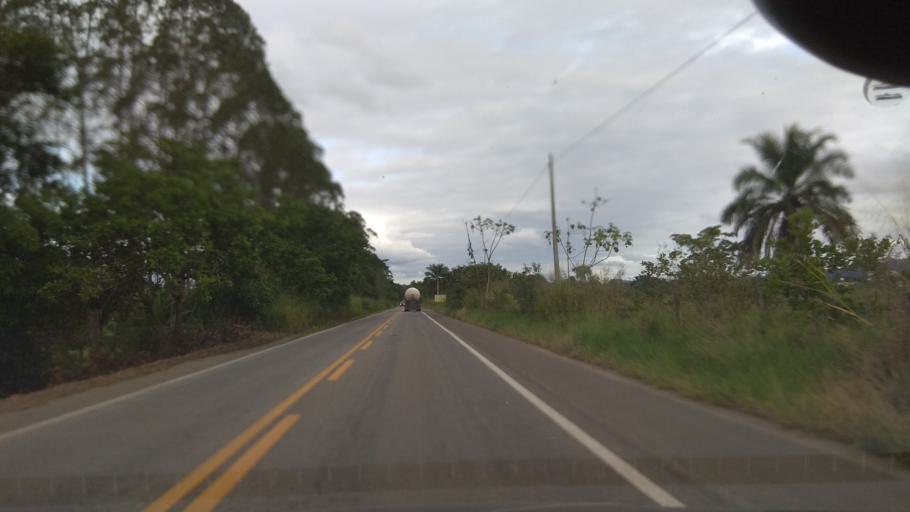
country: BR
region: Bahia
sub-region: Ipiau
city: Ipiau
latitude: -14.1619
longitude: -39.6911
